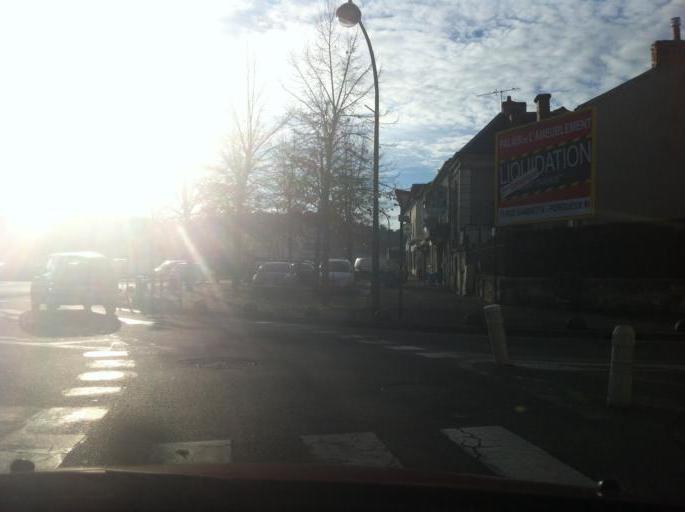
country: FR
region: Aquitaine
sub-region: Departement de la Dordogne
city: Perigueux
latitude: 45.1850
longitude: 0.7107
